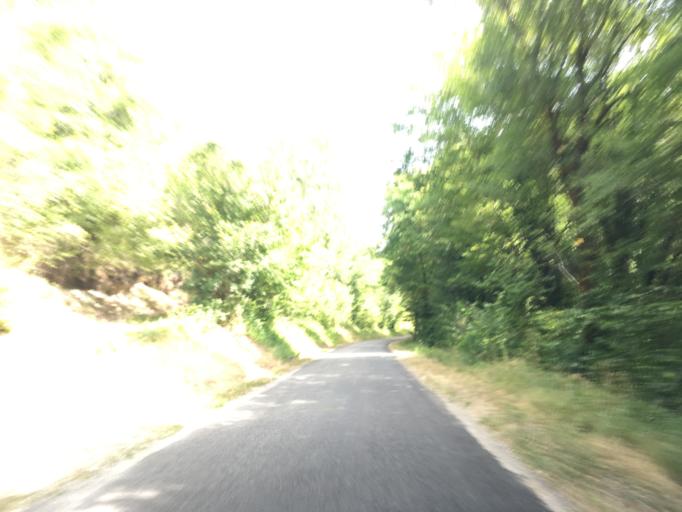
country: FR
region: Midi-Pyrenees
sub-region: Departement du Lot
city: Gramat
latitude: 44.7632
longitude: 1.5793
